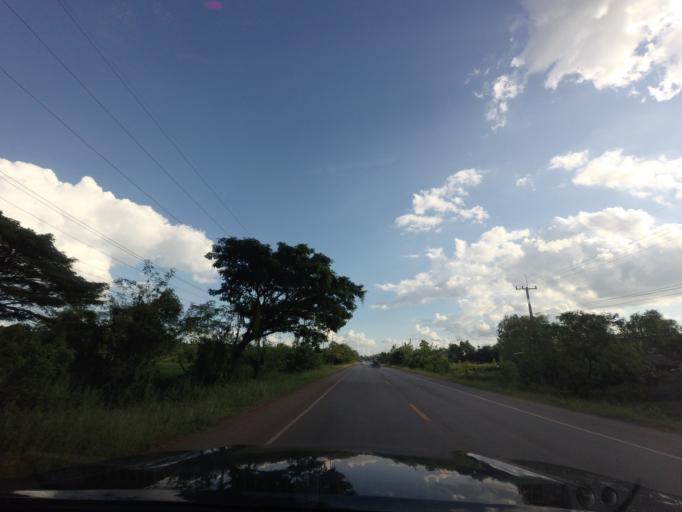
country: TH
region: Changwat Udon Thani
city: Thung Fon
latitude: 17.5056
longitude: 103.2035
